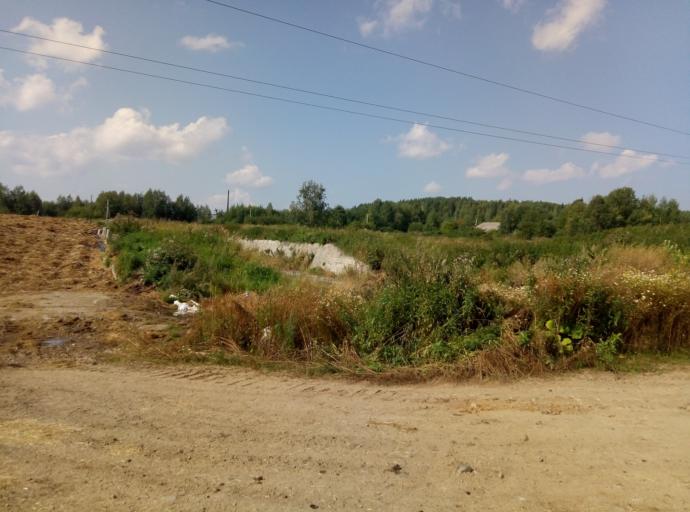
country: RU
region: Sverdlovsk
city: Rudnichnyy
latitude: 59.7171
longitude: 60.2921
